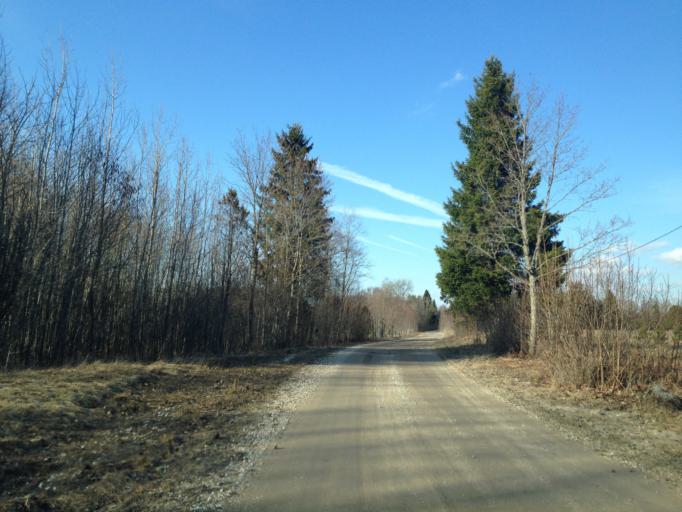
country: EE
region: Harju
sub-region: Nissi vald
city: Turba
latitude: 59.1127
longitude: 24.1578
